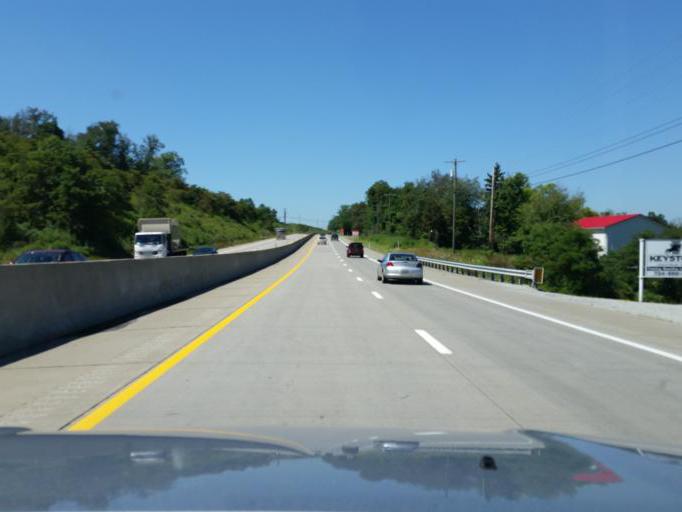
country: US
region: Pennsylvania
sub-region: Westmoreland County
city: Loyalhanna
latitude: 40.4152
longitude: -79.3756
